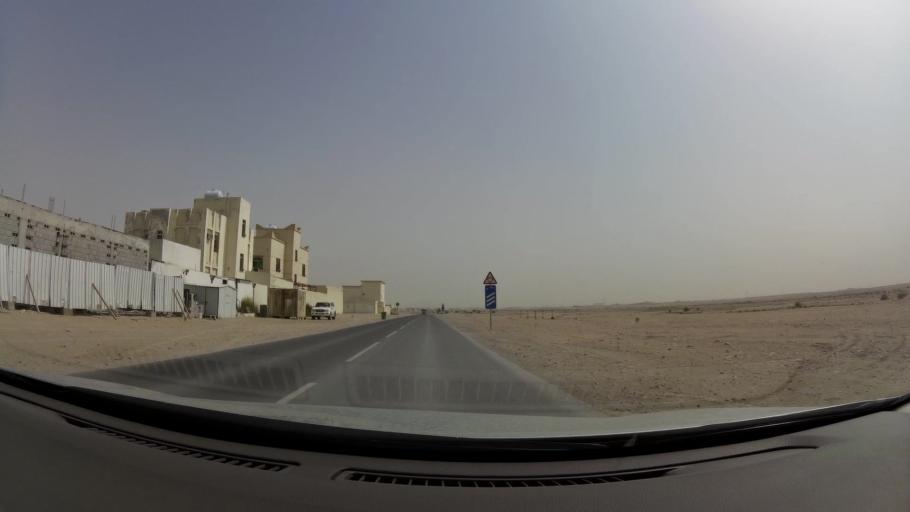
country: QA
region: Baladiyat ar Rayyan
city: Ar Rayyan
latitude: 25.2401
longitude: 51.3653
